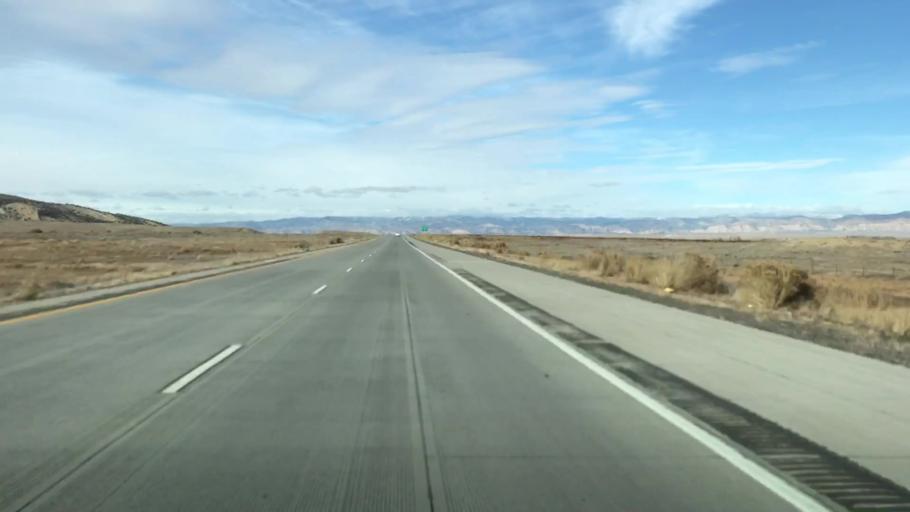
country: US
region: Colorado
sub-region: Mesa County
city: Loma
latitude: 39.1994
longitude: -108.8494
